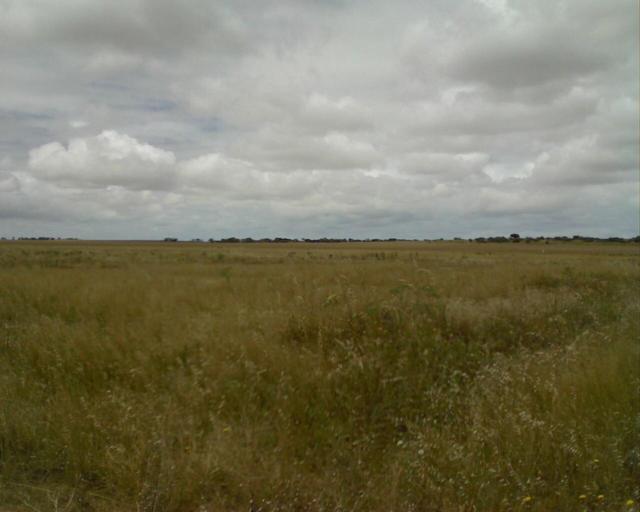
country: AU
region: South Australia
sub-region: Ceduna
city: Ceduna
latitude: -31.9392
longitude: 133.0192
